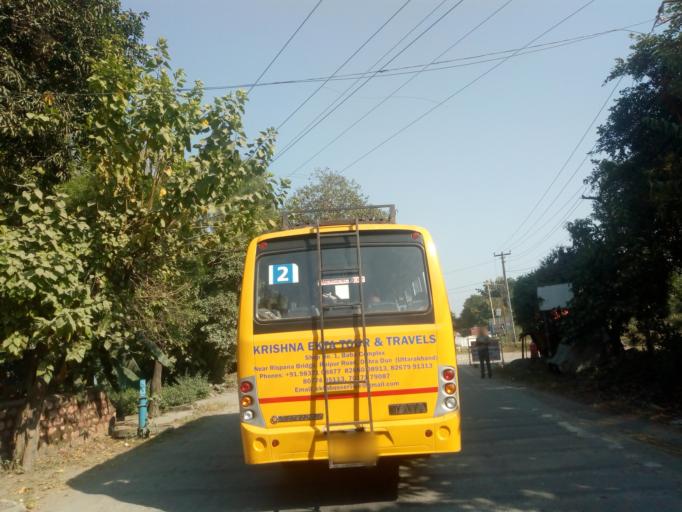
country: IN
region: Uttarakhand
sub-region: Dehradun
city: Harbatpur
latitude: 30.4429
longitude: 77.7029
